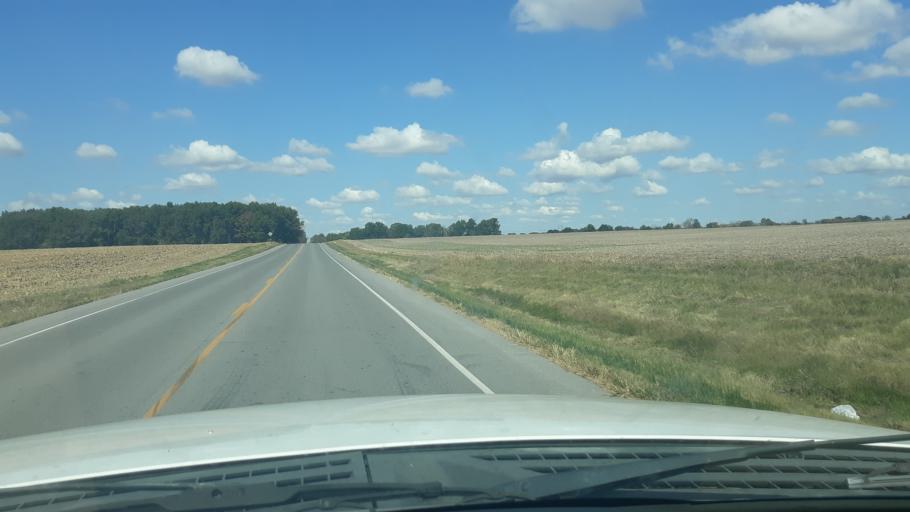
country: US
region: Illinois
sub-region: Saline County
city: Eldorado
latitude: 37.8046
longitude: -88.4847
